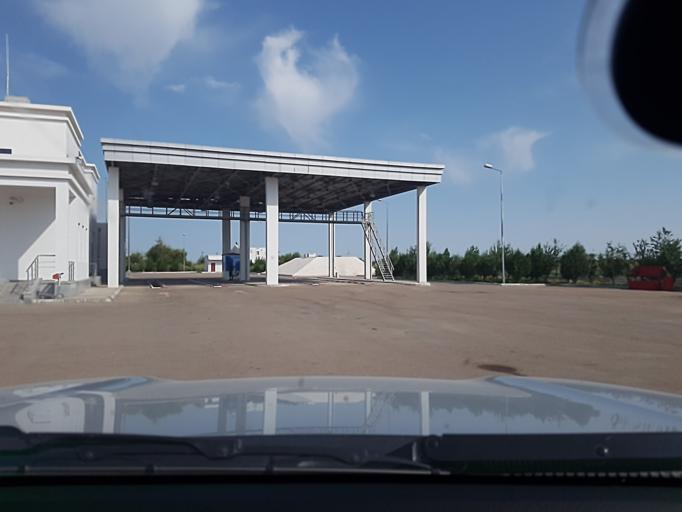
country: TM
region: Dasoguz
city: Dasoguz
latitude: 41.7734
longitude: 60.0584
